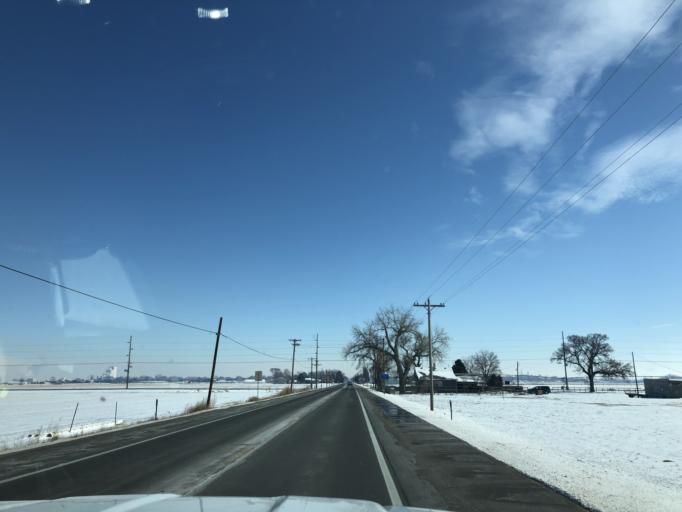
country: US
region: Colorado
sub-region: Morgan County
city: Fort Morgan
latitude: 40.2540
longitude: -103.8320
